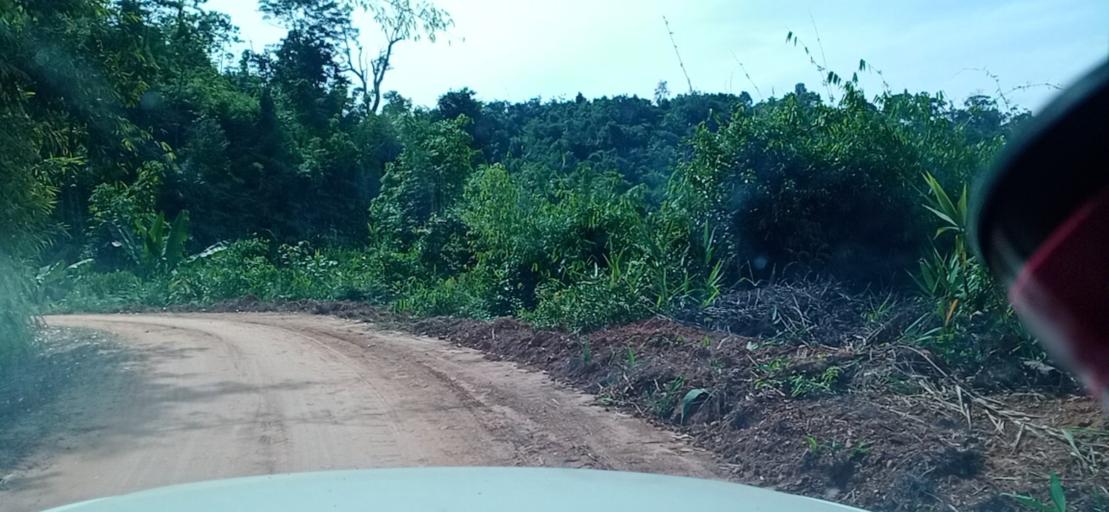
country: TH
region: Changwat Bueng Kan
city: Pak Khat
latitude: 18.6352
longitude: 103.2602
